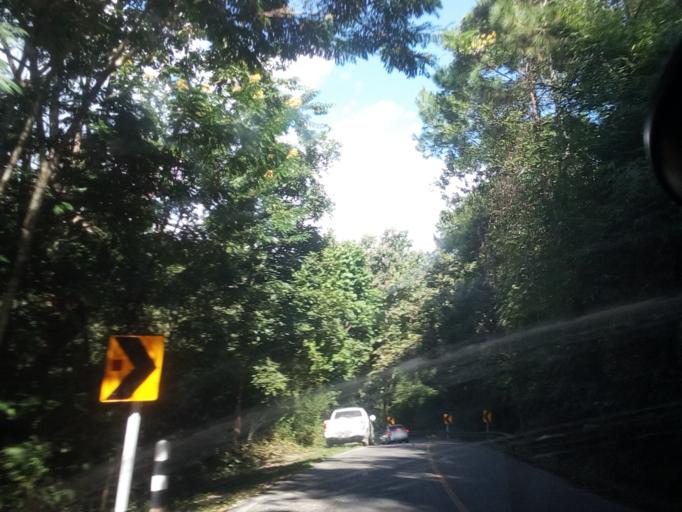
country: TH
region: Chiang Mai
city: Samoeng
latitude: 18.8592
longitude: 98.6508
